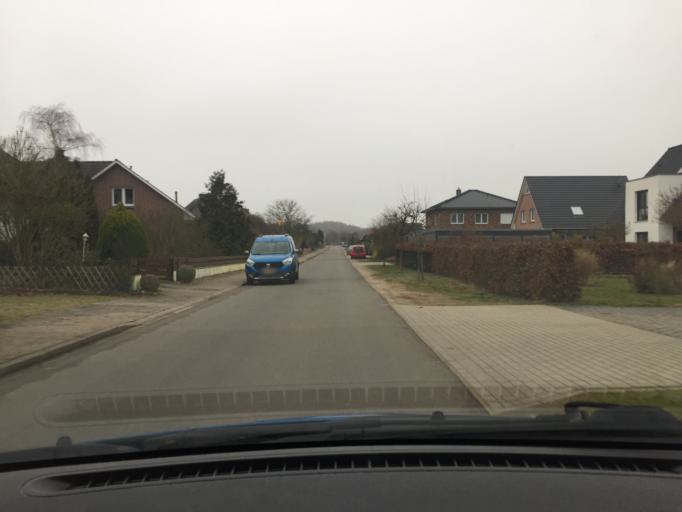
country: DE
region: Lower Saxony
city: Kirchgellersen
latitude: 53.2329
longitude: 10.2823
